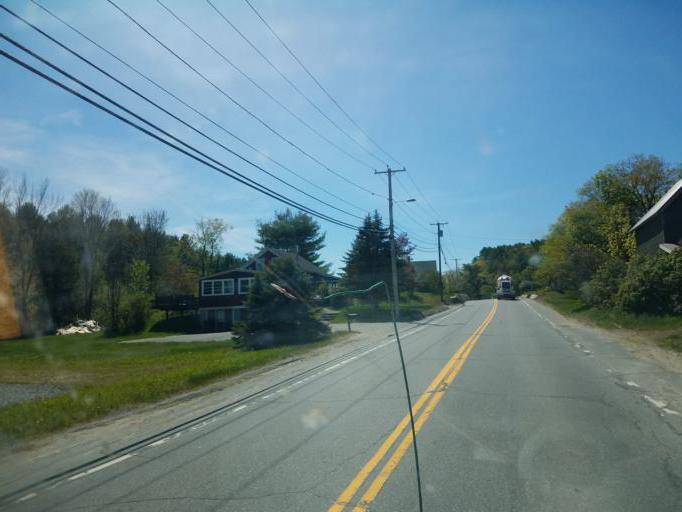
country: US
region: New Hampshire
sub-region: Grafton County
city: Grafton
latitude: 43.6470
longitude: -72.0178
